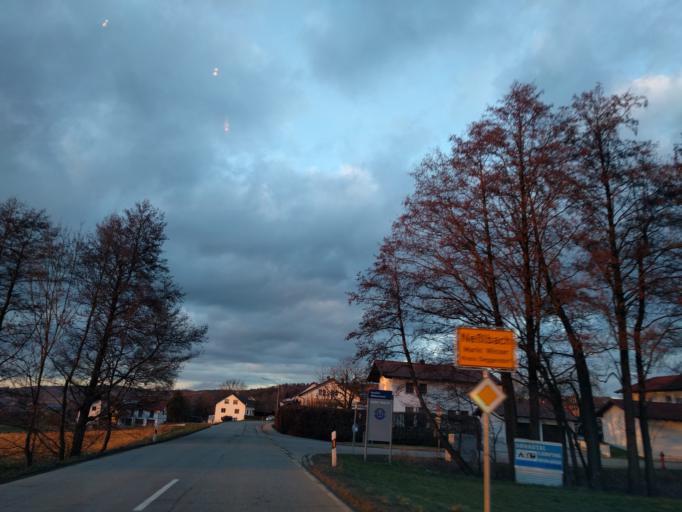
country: DE
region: Bavaria
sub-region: Lower Bavaria
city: Hofkirchen
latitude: 48.6911
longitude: 13.1214
